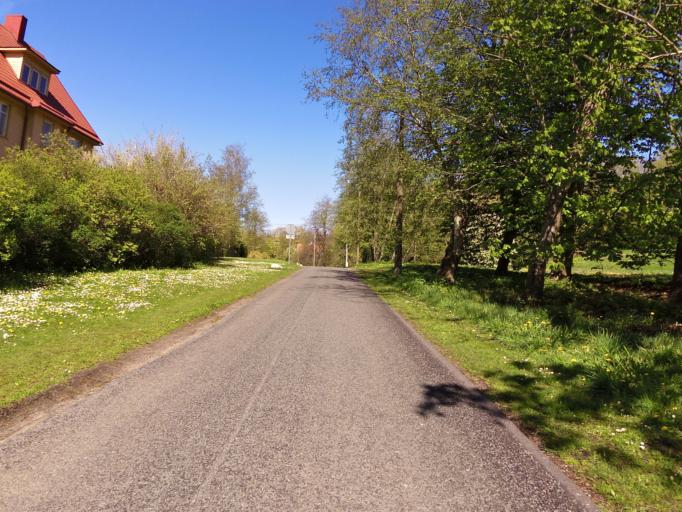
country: EE
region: Harju
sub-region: Tallinna linn
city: Tallinn
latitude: 59.4404
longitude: 24.8031
